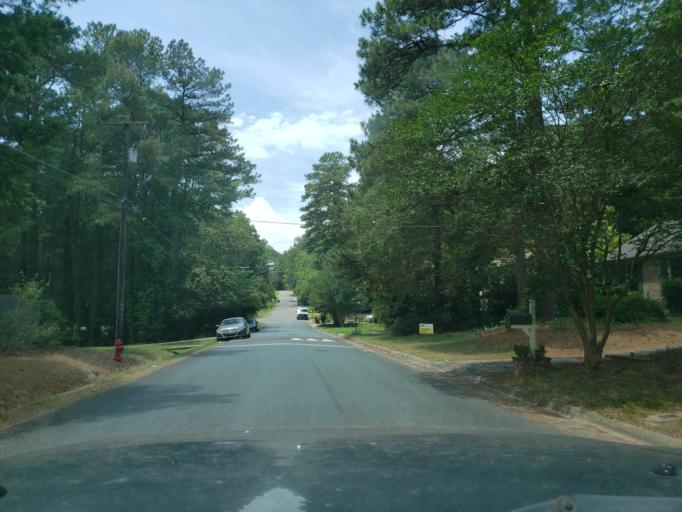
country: US
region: North Carolina
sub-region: Durham County
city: Durham
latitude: 35.9519
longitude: -78.9344
